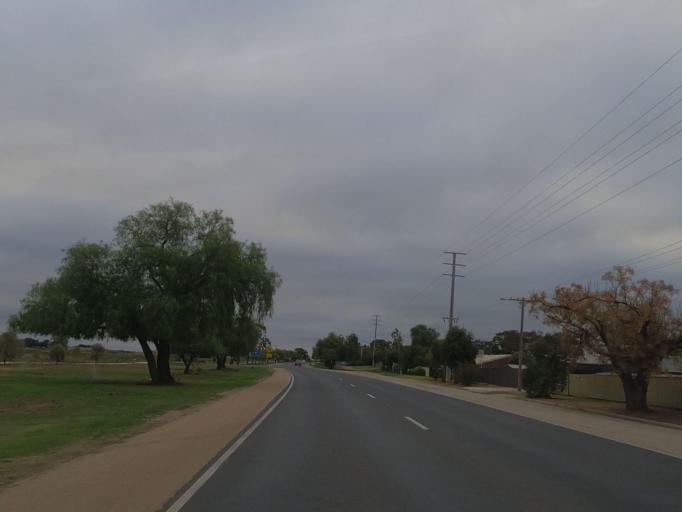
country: AU
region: Victoria
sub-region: Swan Hill
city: Swan Hill
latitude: -35.4586
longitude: 143.6315
